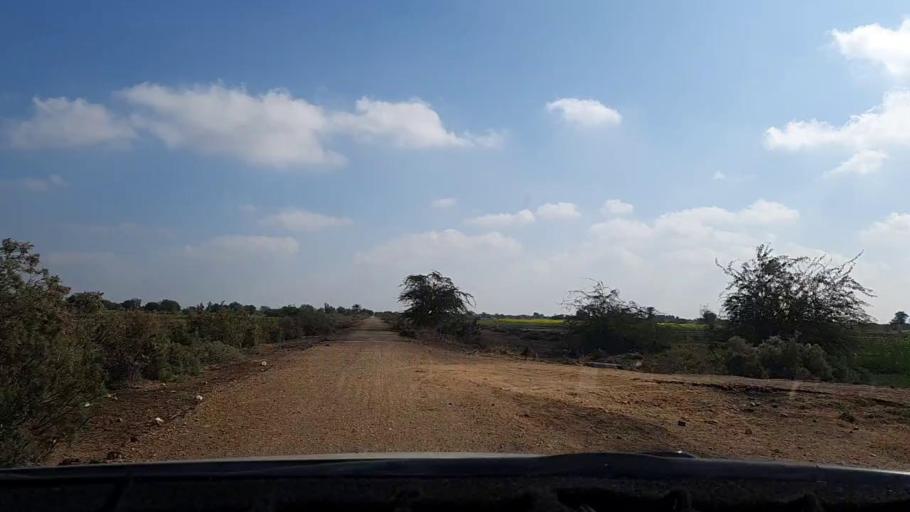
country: PK
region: Sindh
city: Pithoro
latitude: 25.7254
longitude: 69.2905
